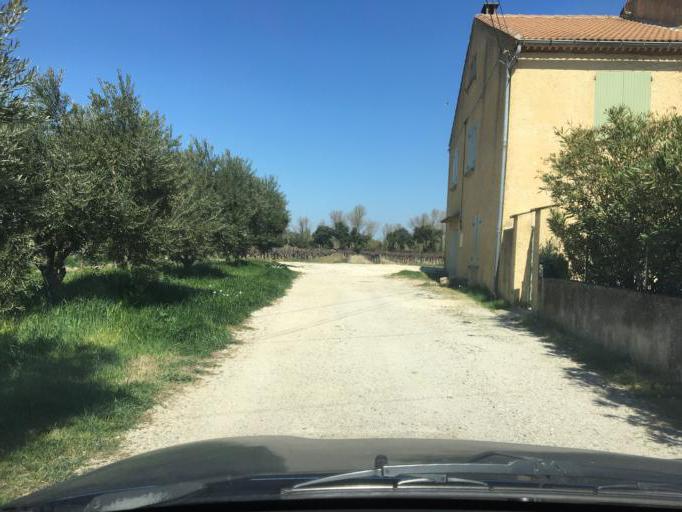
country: FR
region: Provence-Alpes-Cote d'Azur
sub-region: Departement du Vaucluse
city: Serignan-du-Comtat
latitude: 44.1750
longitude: 4.8453
